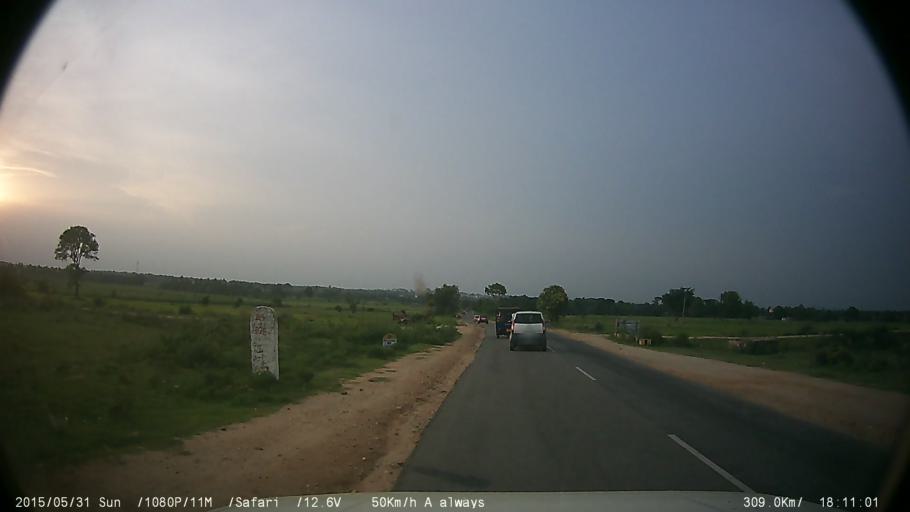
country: IN
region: Karnataka
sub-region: Mysore
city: Nanjangud
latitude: 12.0841
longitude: 76.6748
